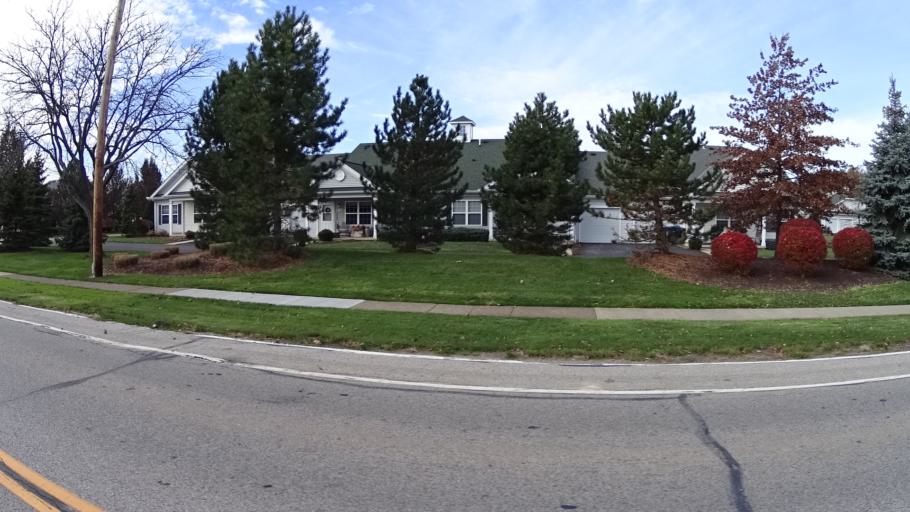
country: US
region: Ohio
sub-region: Lorain County
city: Avon Lake
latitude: 41.4957
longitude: -82.0616
